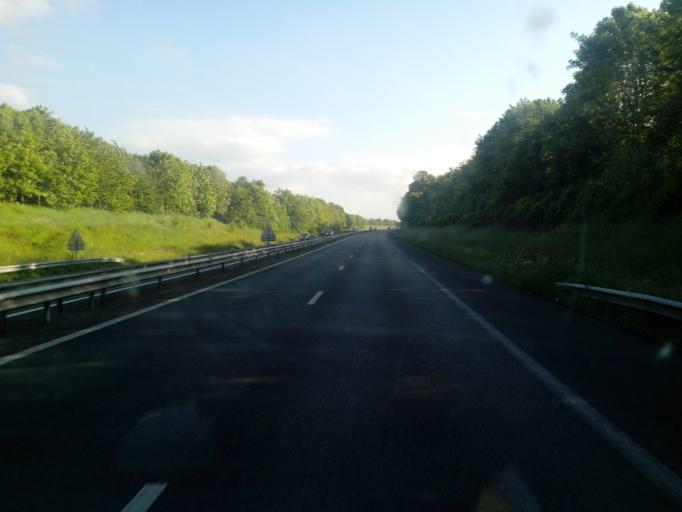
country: FR
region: Lower Normandy
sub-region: Departement du Calvados
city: Grainville-sur-Odon
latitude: 49.1277
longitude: -0.5691
